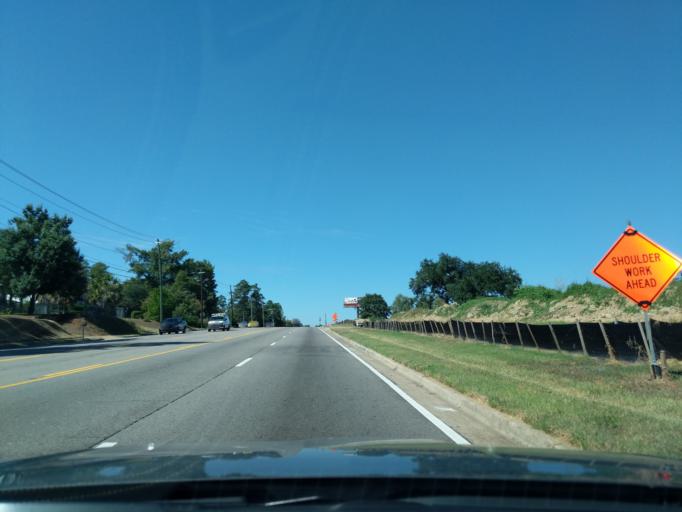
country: US
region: South Carolina
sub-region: Aiken County
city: North Augusta
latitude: 33.5004
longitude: -82.0126
